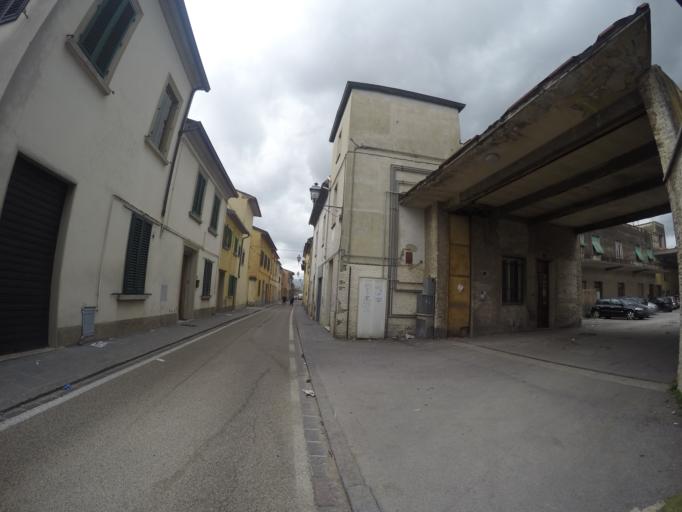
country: IT
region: Tuscany
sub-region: Provincia di Prato
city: Prato
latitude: 43.8877
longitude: 11.0560
